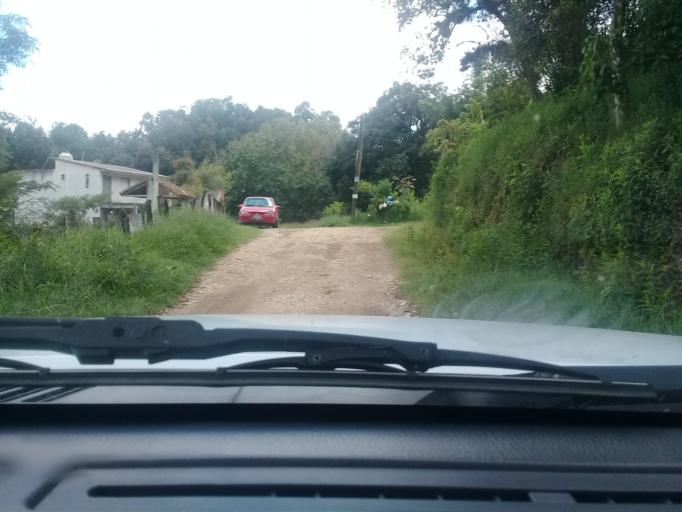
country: MX
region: Veracruz
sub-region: Tlalnelhuayocan
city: Otilpan
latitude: 19.5444
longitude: -96.9760
